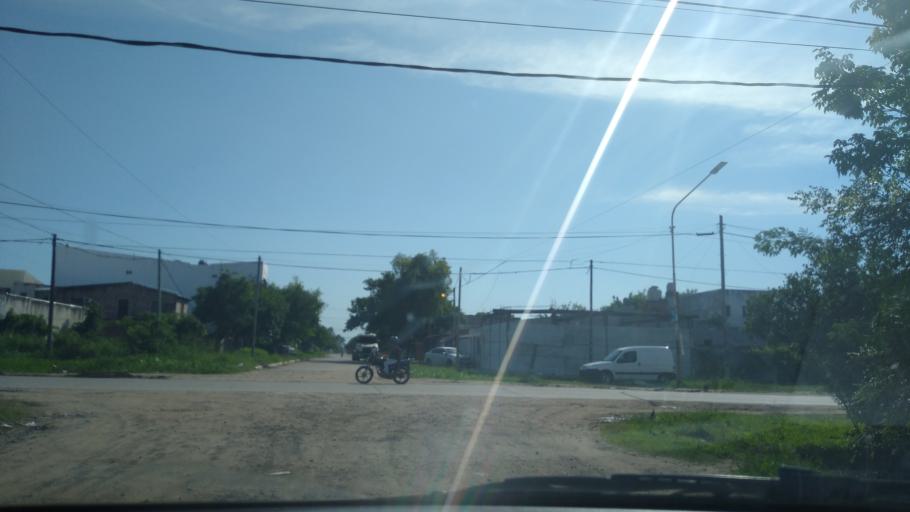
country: AR
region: Chaco
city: Barranqueras
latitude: -27.4854
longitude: -58.9476
